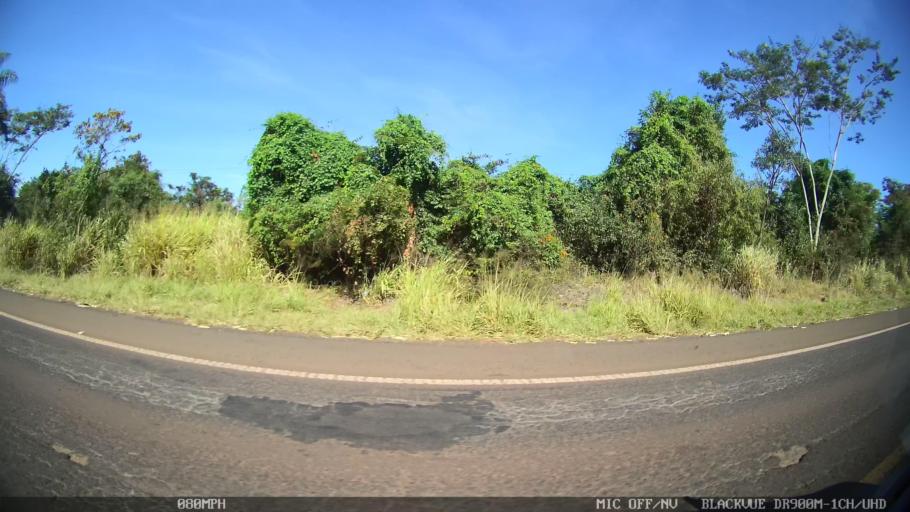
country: BR
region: Sao Paulo
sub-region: Barretos
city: Barretos
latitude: -20.5498
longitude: -48.6319
